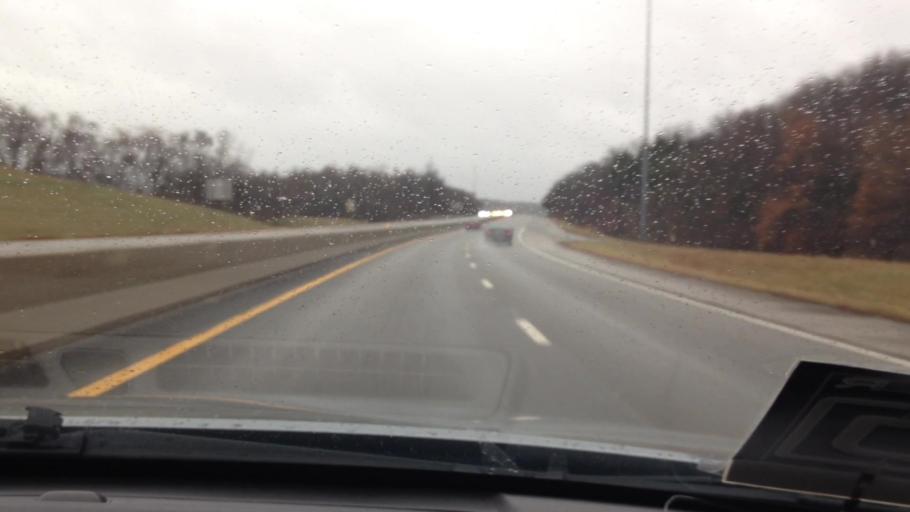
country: US
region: Kansas
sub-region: Johnson County
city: Roeland Park
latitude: 39.0607
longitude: -94.6467
